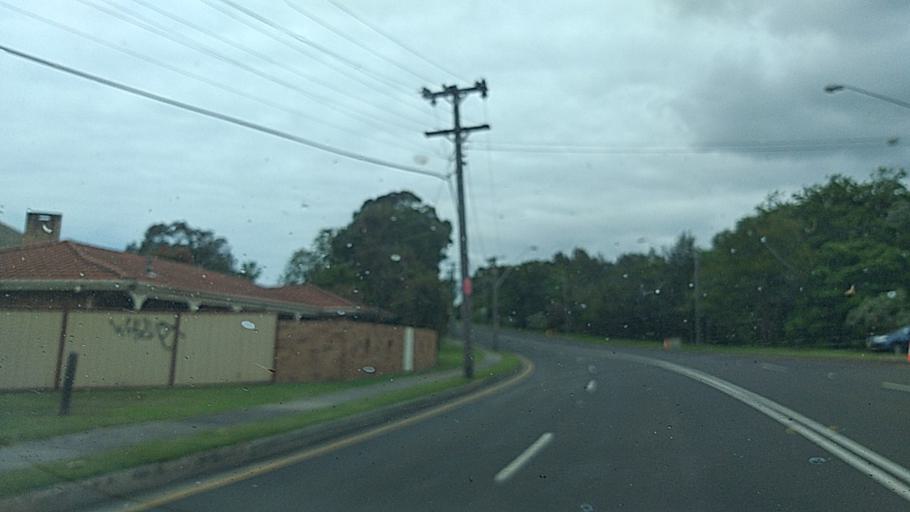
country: AU
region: New South Wales
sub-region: Wollongong
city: Bulli
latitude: -34.3509
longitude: 150.9029
